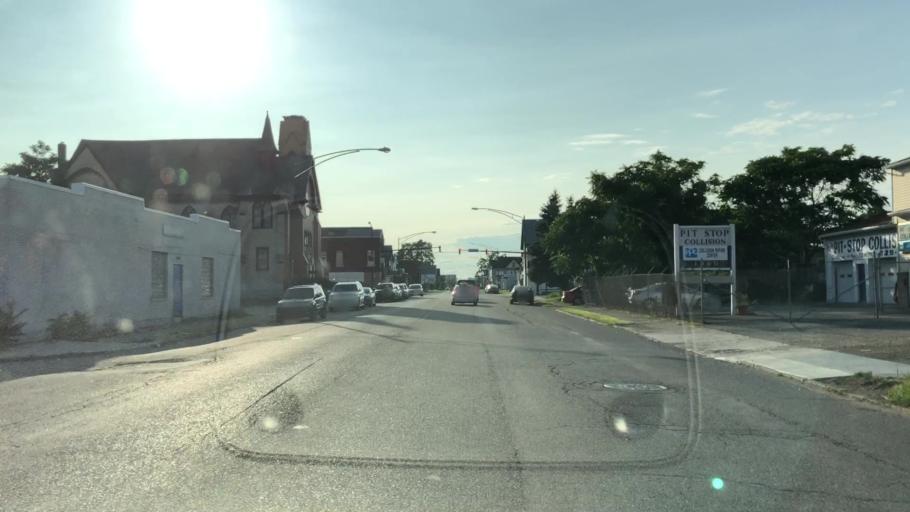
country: US
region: New York
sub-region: Erie County
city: West Seneca
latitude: 42.8741
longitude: -78.8252
